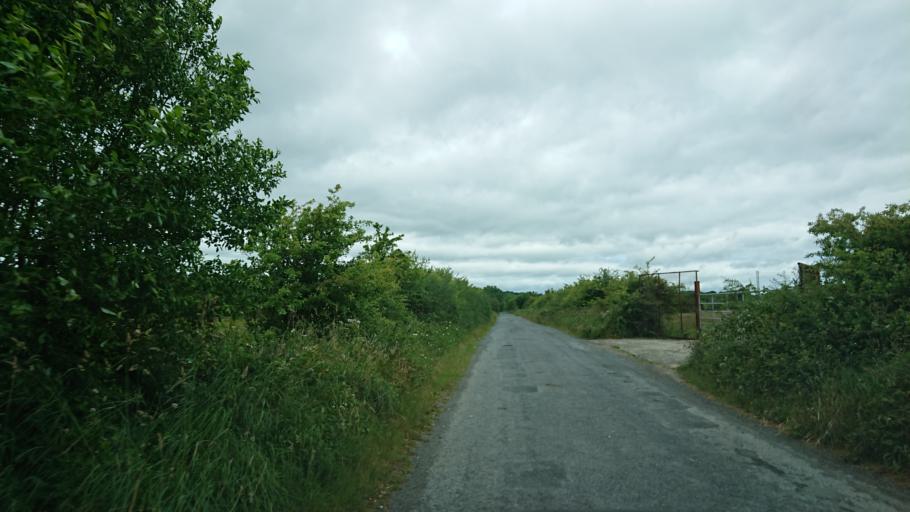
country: IE
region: Munster
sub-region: Waterford
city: Waterford
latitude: 52.2200
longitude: -7.1416
